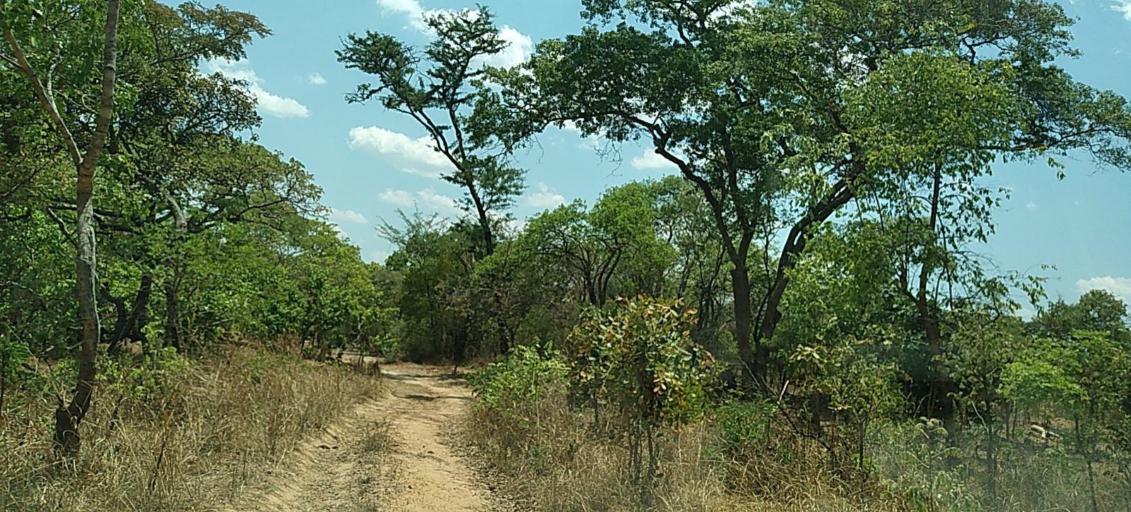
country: ZM
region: Central
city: Kapiri Mposhi
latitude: -13.6279
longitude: 28.7775
